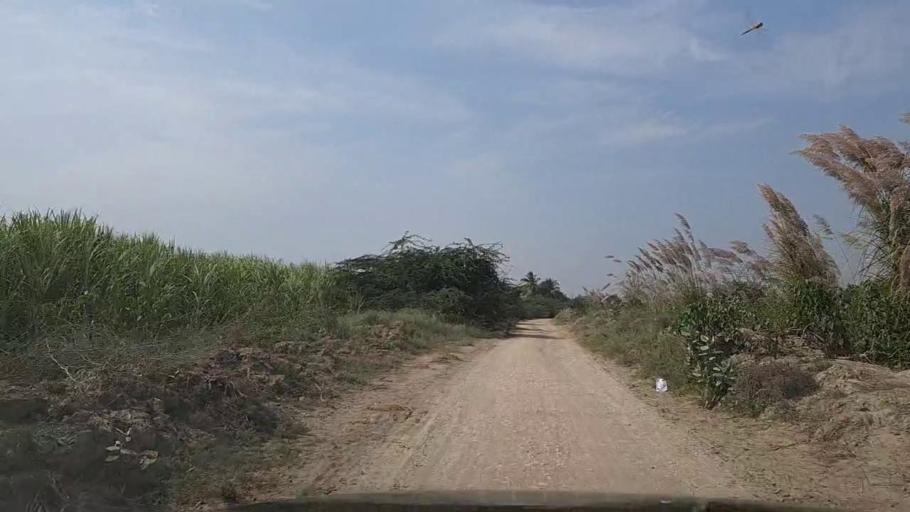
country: PK
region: Sindh
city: Thatta
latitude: 24.7988
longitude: 67.8842
